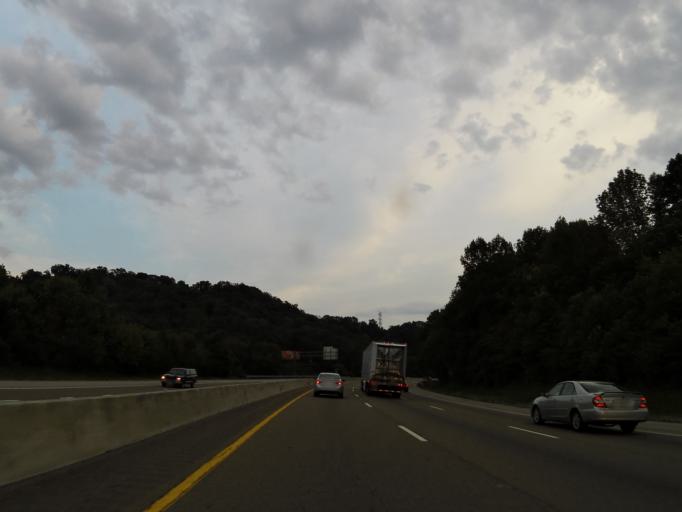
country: US
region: Tennessee
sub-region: Knox County
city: Knoxville
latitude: 36.0412
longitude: -83.9969
